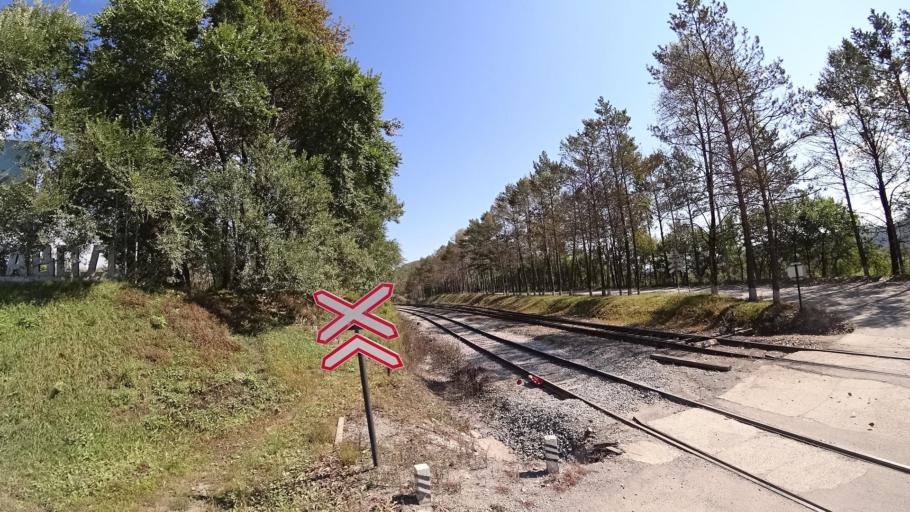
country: RU
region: Jewish Autonomous Oblast
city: Londoko
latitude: 49.0019
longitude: 131.8880
